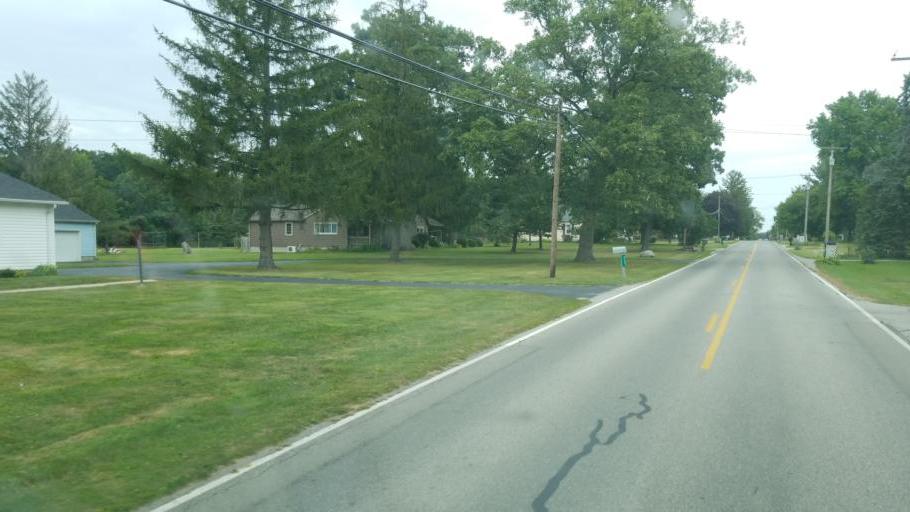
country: US
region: Ohio
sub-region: Marion County
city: Marion
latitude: 40.5427
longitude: -83.1369
